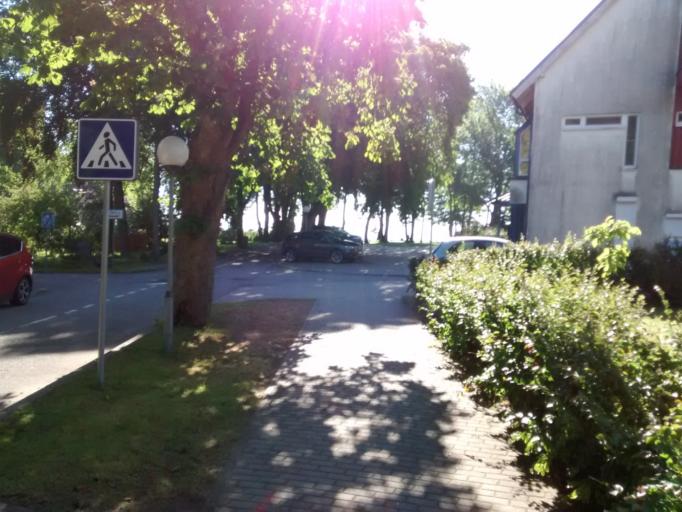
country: LT
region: Klaipedos apskritis
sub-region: Klaipeda
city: Klaipeda
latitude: 55.5440
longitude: 21.1213
